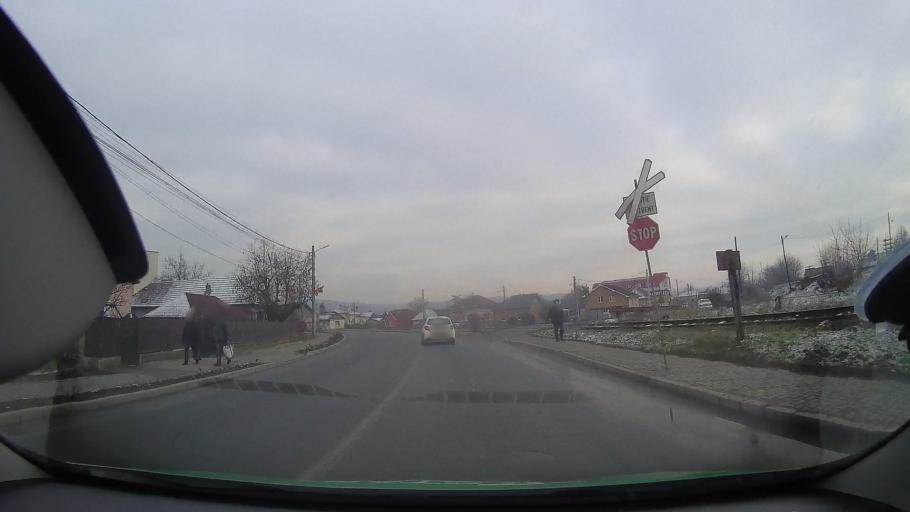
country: RO
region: Mures
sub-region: Comuna Ludus
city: Ludus
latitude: 46.4695
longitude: 24.0943
